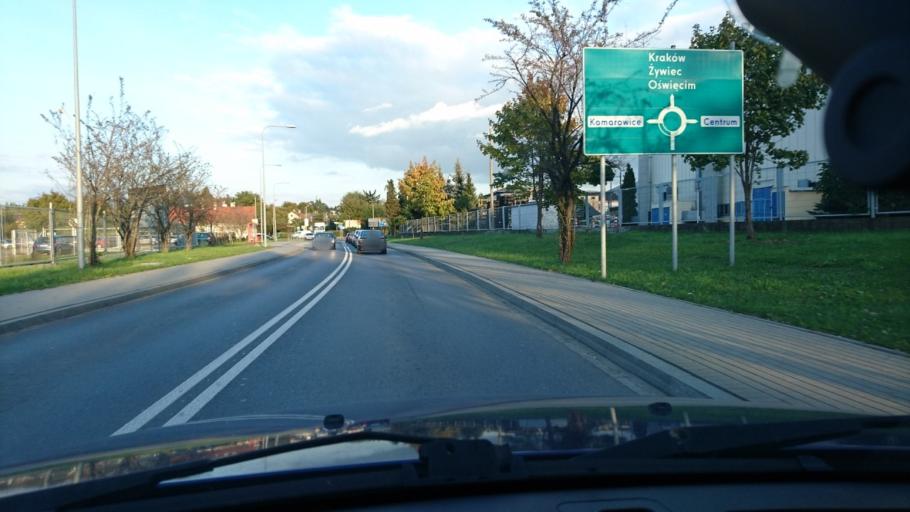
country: PL
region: Silesian Voivodeship
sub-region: Bielsko-Biala
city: Bielsko-Biala
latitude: 49.8406
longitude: 19.0498
